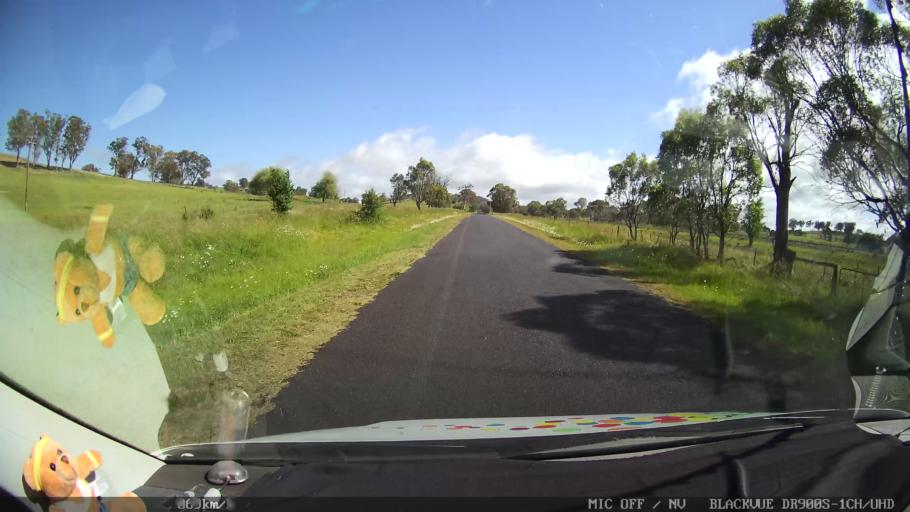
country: AU
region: New South Wales
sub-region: Guyra
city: Guyra
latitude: -30.0465
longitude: 151.6668
